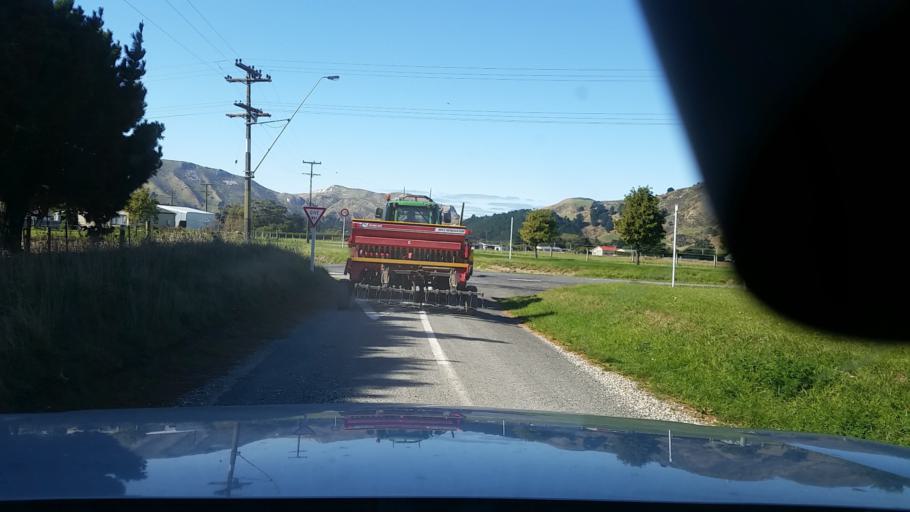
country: NZ
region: Marlborough
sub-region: Marlborough District
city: Blenheim
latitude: -41.8254
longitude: 174.1337
